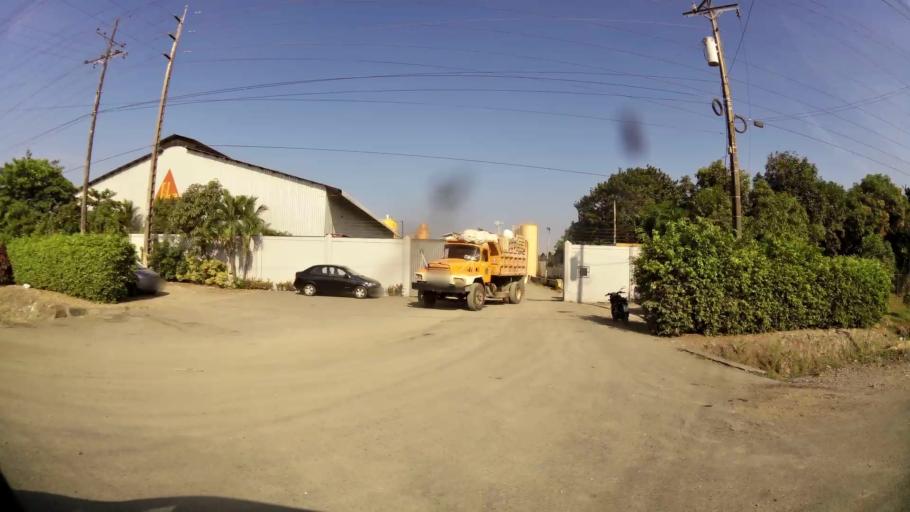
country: EC
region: Guayas
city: Eloy Alfaro
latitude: -2.1825
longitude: -79.8292
